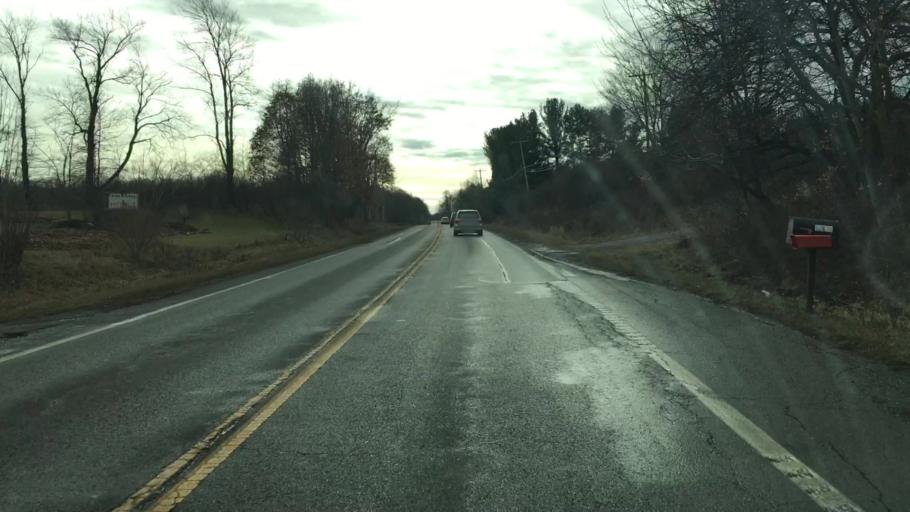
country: US
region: Ohio
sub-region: Columbiana County
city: Salem
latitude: 40.9357
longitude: -80.8403
